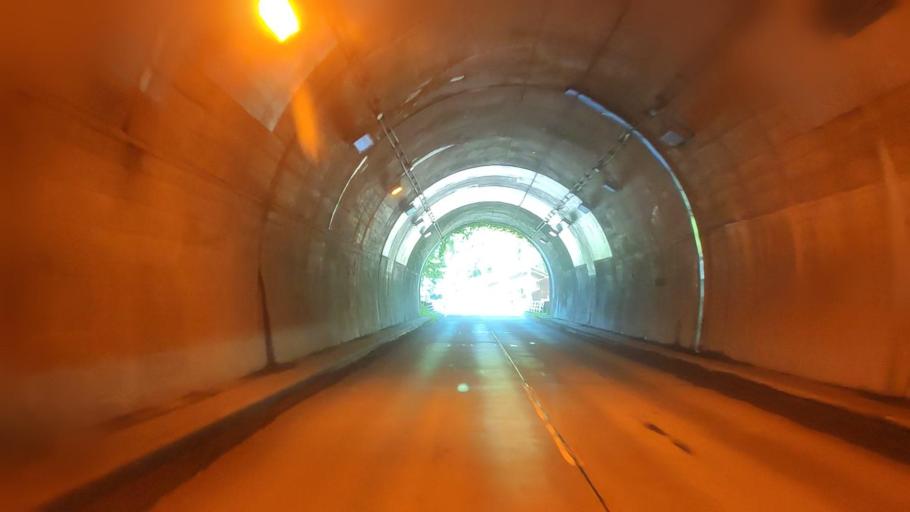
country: JP
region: Nara
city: Yoshino-cho
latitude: 34.4076
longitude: 135.9305
